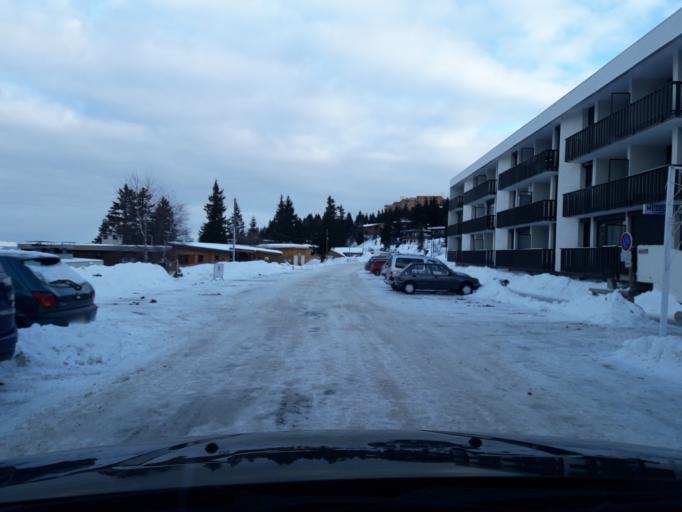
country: FR
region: Rhone-Alpes
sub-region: Departement de l'Isere
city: Vaulnaveys-le-Bas
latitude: 45.1116
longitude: 5.8759
